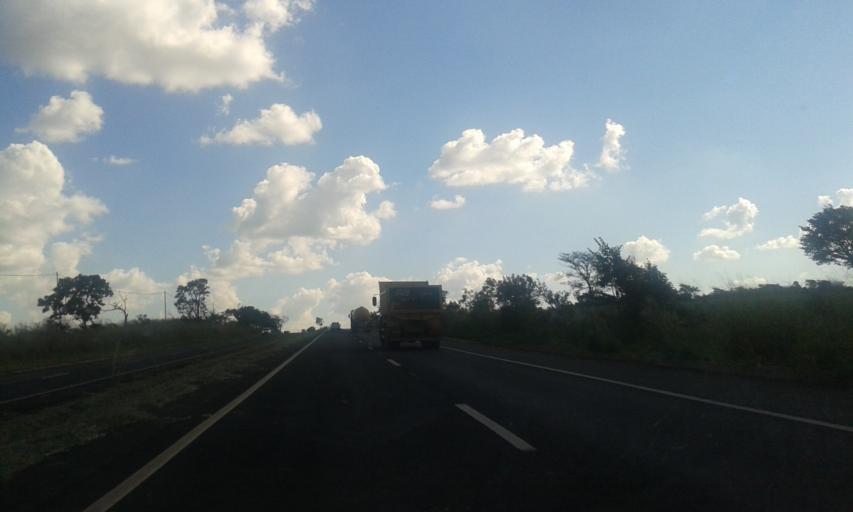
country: BR
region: Minas Gerais
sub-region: Monte Alegre De Minas
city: Monte Alegre de Minas
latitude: -18.8911
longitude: -48.6776
